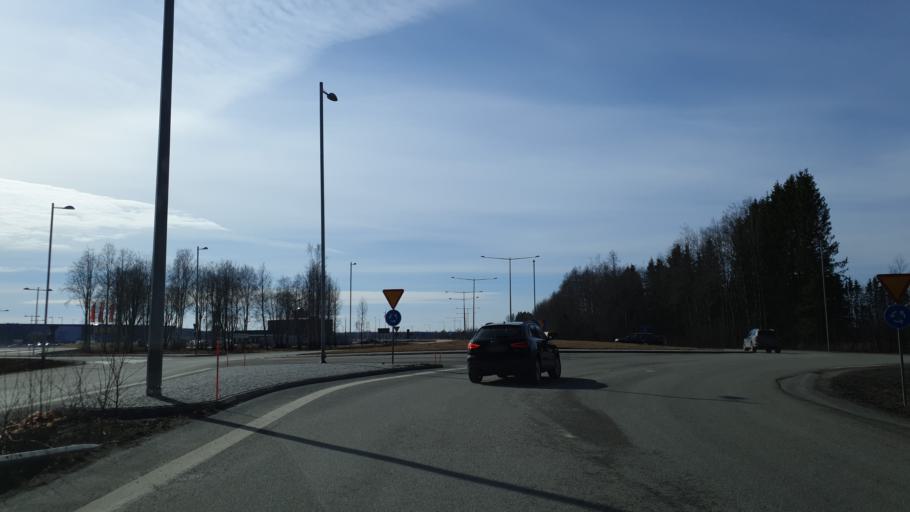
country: SE
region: Vaesterbotten
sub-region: Umea Kommun
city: Umea
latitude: 63.8123
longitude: 20.2493
